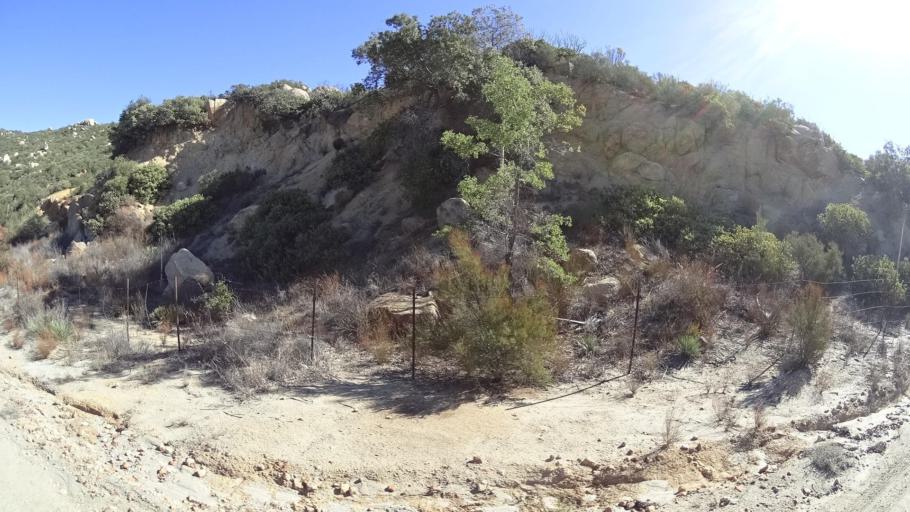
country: US
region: California
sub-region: San Diego County
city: Descanso
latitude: 32.8662
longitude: -116.6517
